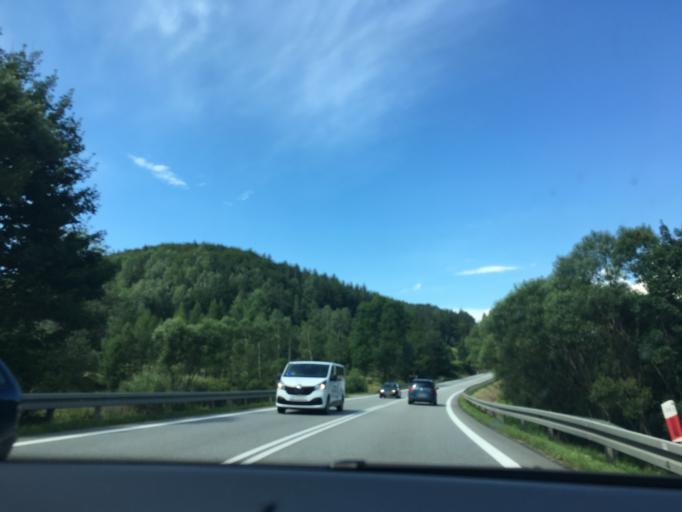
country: PL
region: Subcarpathian Voivodeship
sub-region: Powiat krosnienski
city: Dukla
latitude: 49.4449
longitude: 21.6904
